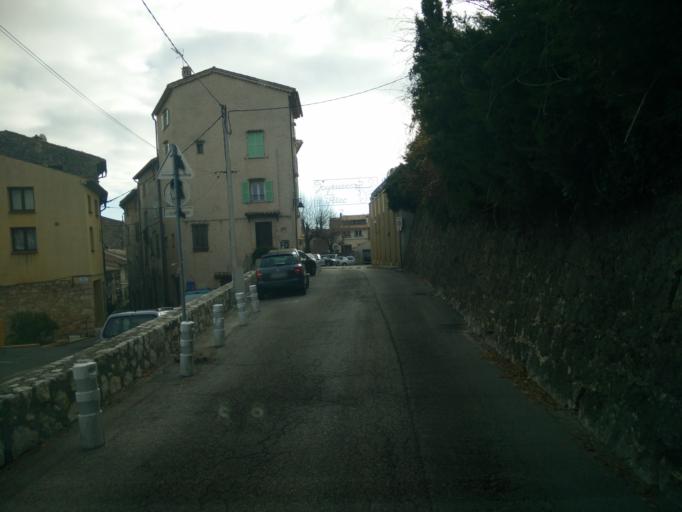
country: FR
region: Provence-Alpes-Cote d'Azur
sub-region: Departement des Alpes-Maritimes
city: Le Broc
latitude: 43.8097
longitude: 7.1681
